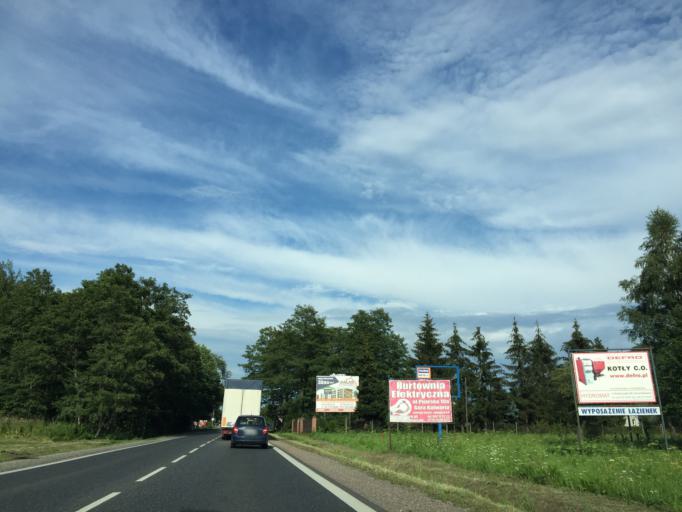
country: PL
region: Masovian Voivodeship
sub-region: Powiat piaseczynski
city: Gora Kalwaria
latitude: 51.9724
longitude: 21.2014
